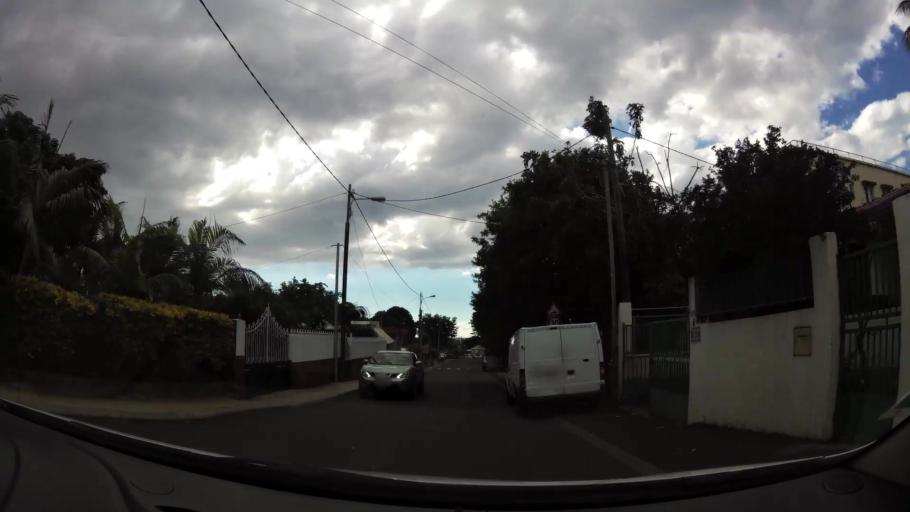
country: RE
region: Reunion
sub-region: Reunion
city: Saint-Denis
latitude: -20.8908
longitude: 55.4743
